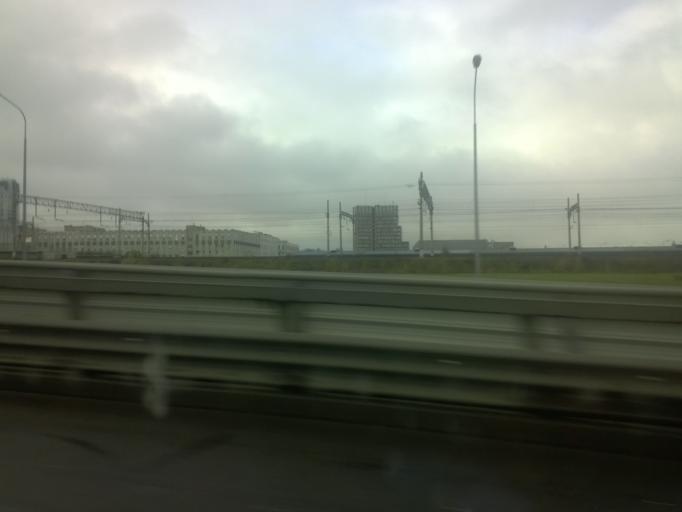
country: RU
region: St.-Petersburg
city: Avtovo
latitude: 59.8546
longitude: 30.2905
